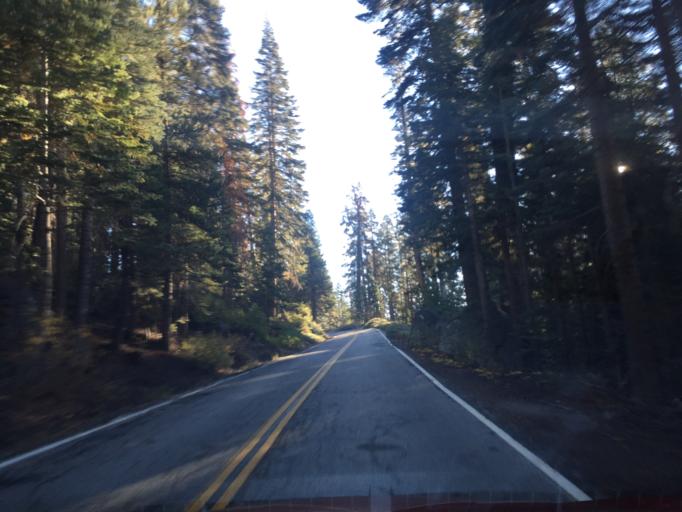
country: US
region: California
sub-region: Mariposa County
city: Yosemite Valley
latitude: 37.6906
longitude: -119.5891
